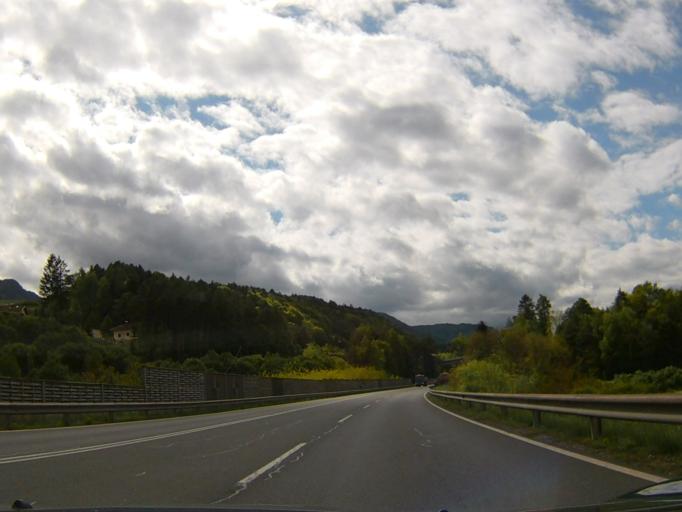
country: AT
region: Carinthia
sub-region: Politischer Bezirk Villach Land
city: Fresach
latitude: 46.6593
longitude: 13.7526
